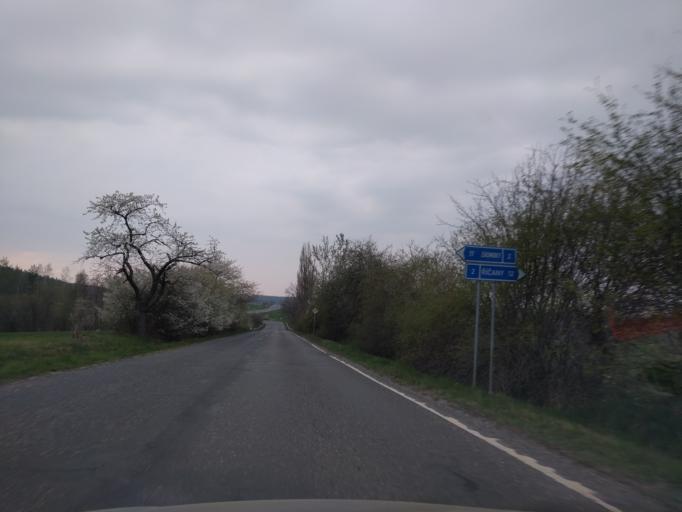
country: CZ
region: Central Bohemia
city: Kostelec nad Cernymi Lesy
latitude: 49.9928
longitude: 14.8355
